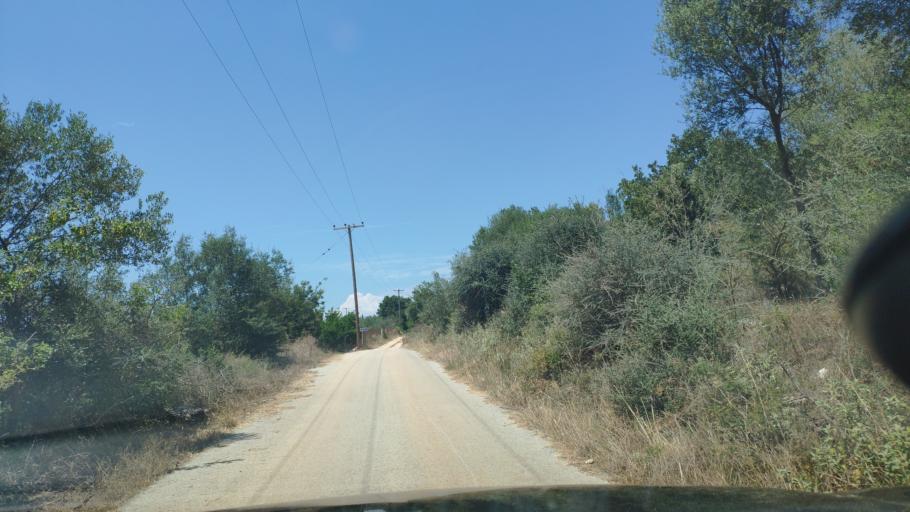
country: GR
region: West Greece
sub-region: Nomos Aitolias kai Akarnanias
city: Amfilochia
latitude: 38.9068
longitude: 21.1049
